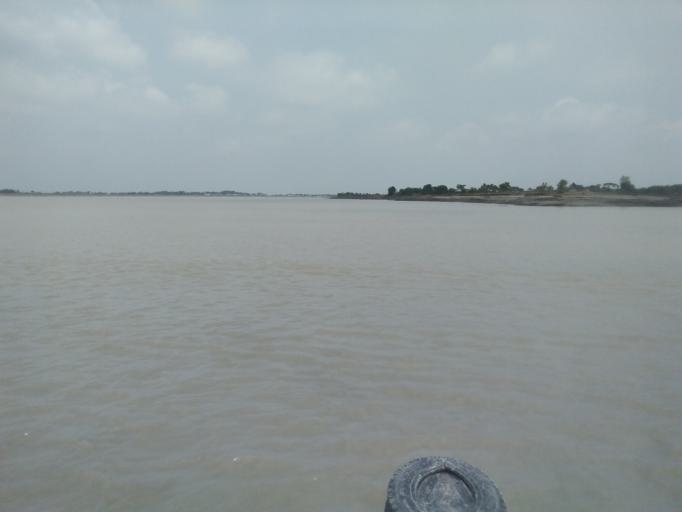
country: BD
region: Khulna
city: Phultala
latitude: 22.6443
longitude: 89.4116
